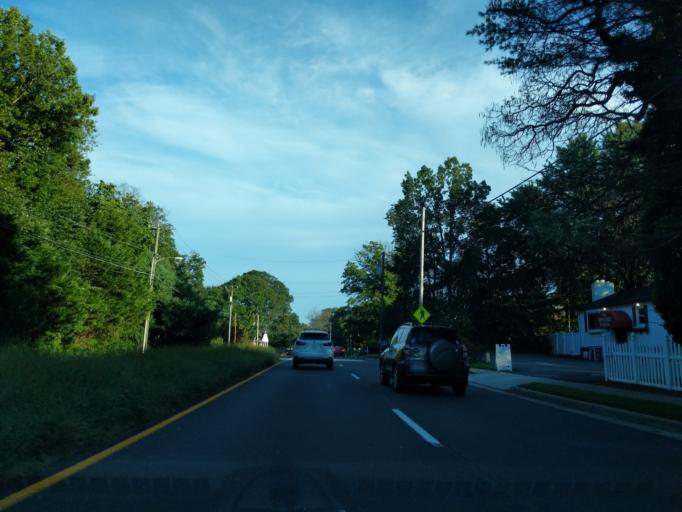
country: US
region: Virginia
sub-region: Fairfax County
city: Oakton
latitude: 38.8725
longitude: -77.2806
